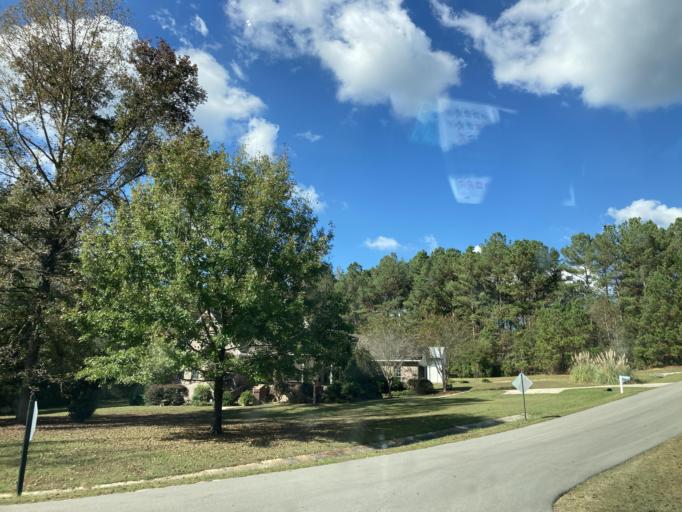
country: US
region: Mississippi
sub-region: Lamar County
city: Sumrall
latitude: 31.3650
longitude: -89.5130
